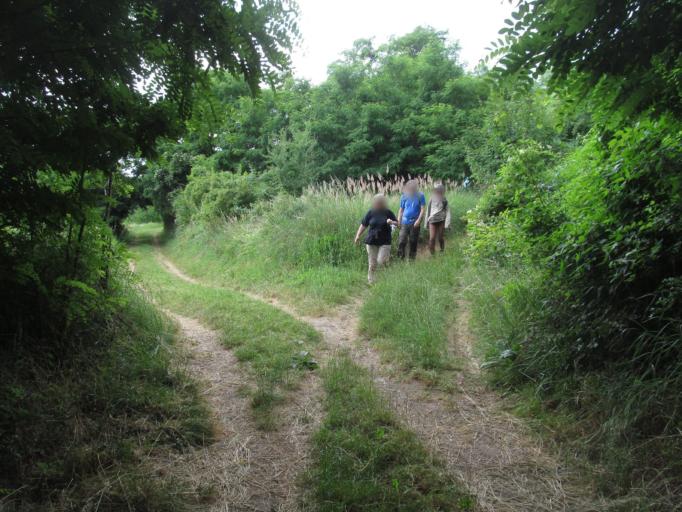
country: HU
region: Veszprem
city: Badacsonytomaj
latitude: 46.8760
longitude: 17.5316
